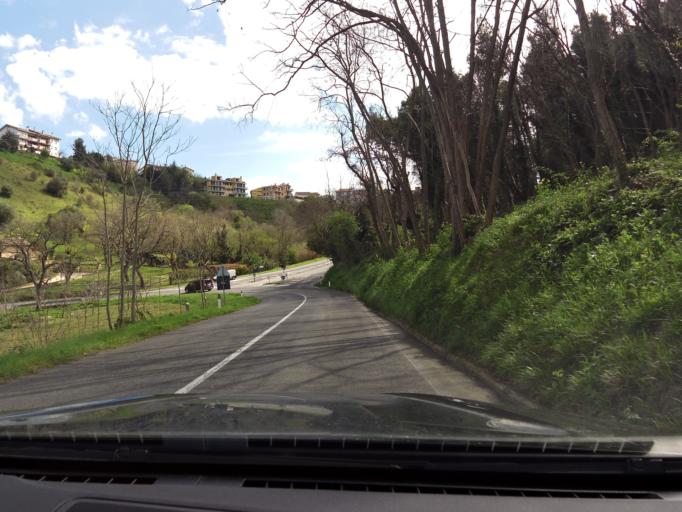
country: IT
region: The Marches
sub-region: Provincia di Ancona
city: Castelfidardo
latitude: 43.4722
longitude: 13.5515
